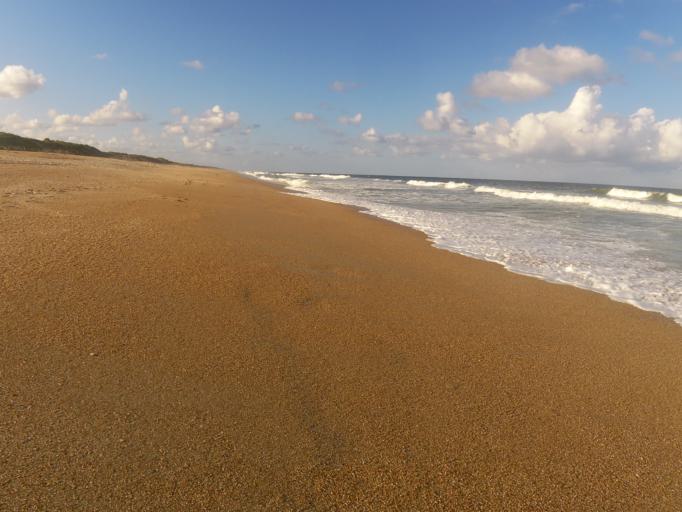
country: US
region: Florida
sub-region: Saint Johns County
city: Palm Valley
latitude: 30.0987
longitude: -81.3402
